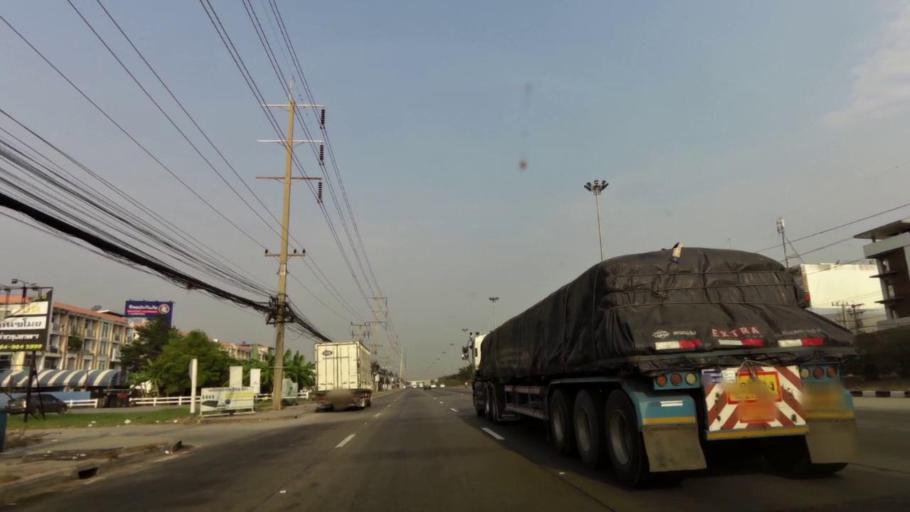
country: TH
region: Phra Nakhon Si Ayutthaya
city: Uthai
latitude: 14.3243
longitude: 100.6292
